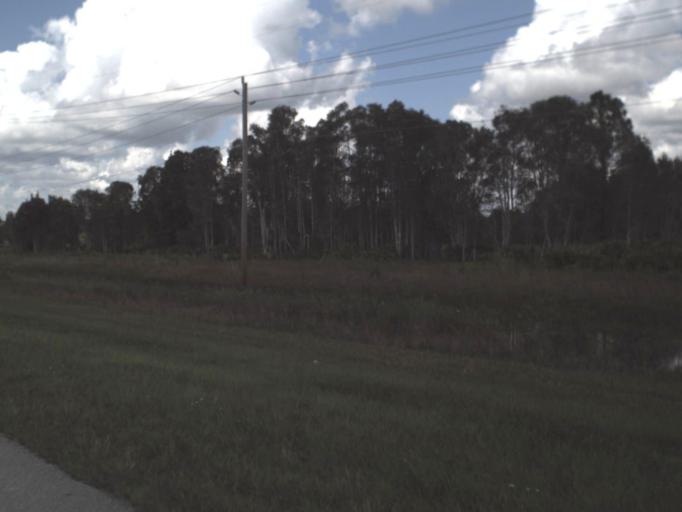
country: US
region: Florida
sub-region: Lee County
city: Gateway
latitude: 26.5704
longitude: -81.6876
